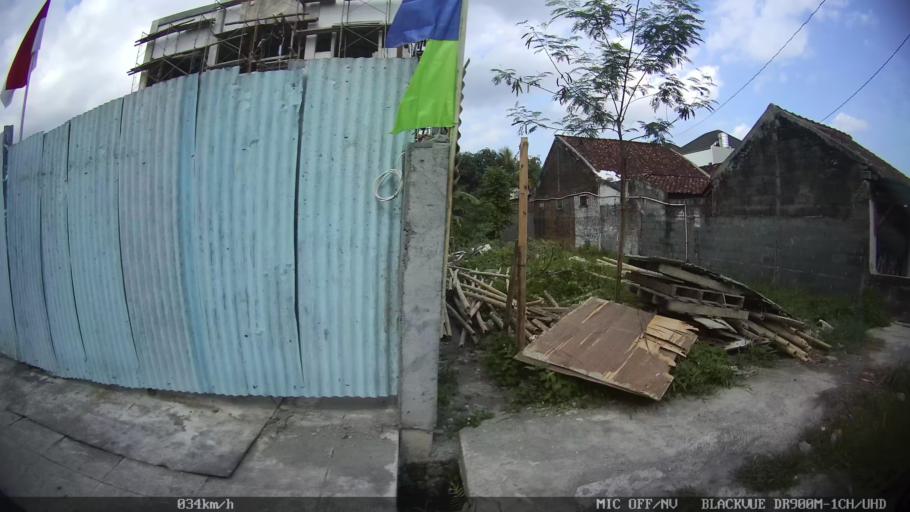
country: ID
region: Daerah Istimewa Yogyakarta
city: Gamping Lor
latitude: -7.7926
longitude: 110.3366
